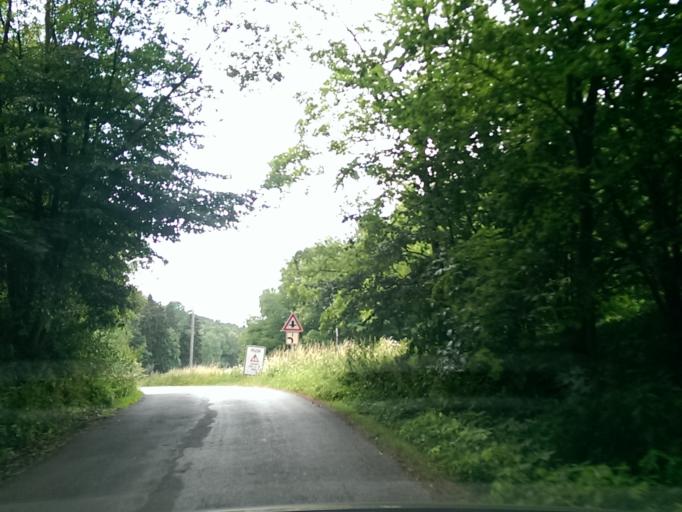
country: CZ
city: Duba
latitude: 50.4719
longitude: 14.5273
